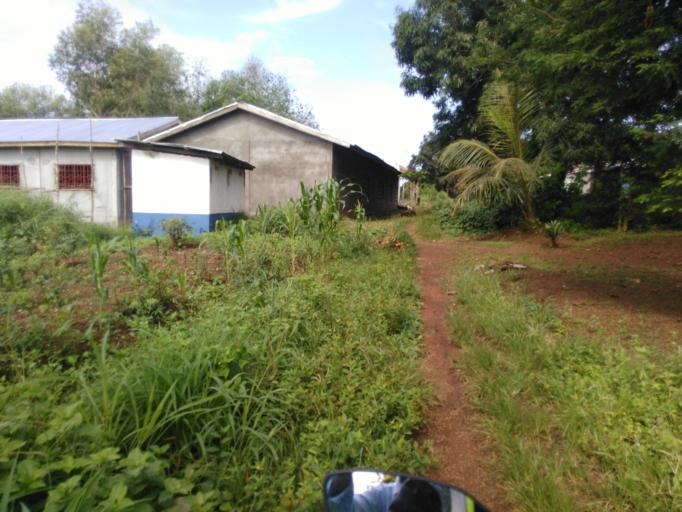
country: SL
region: Southern Province
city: Rotifunk
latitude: 8.4863
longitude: -12.7551
